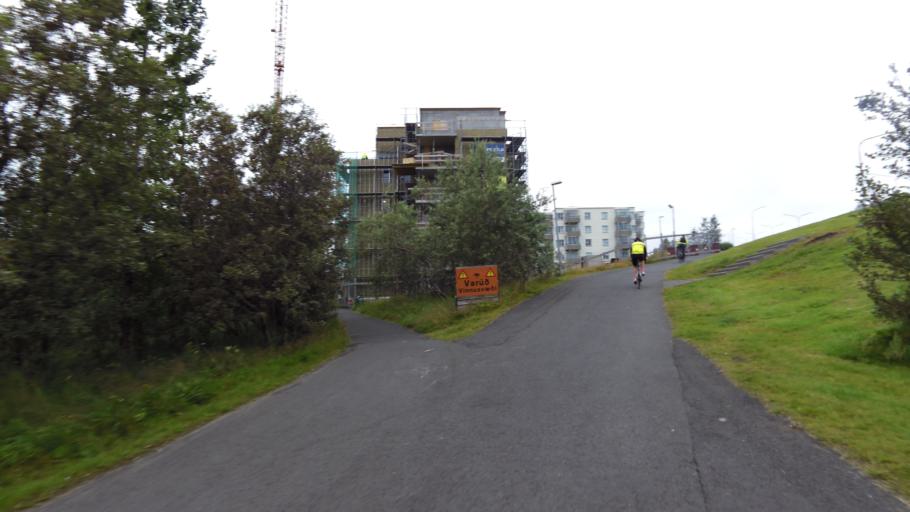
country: IS
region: Capital Region
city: Kopavogur
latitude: 64.1069
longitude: -21.9059
